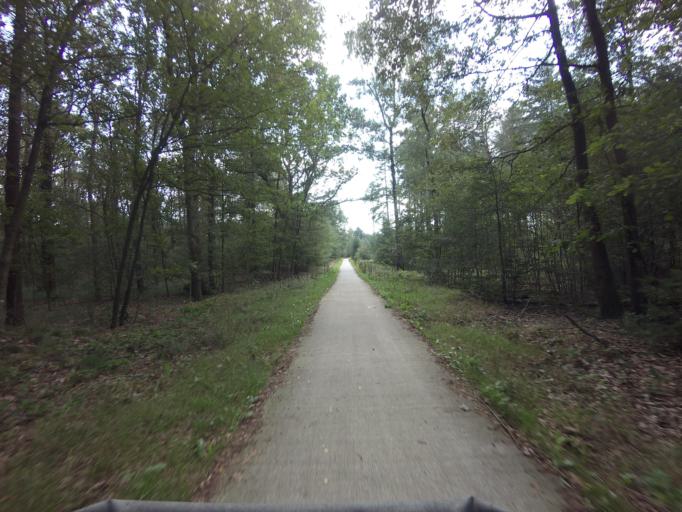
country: NL
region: Drenthe
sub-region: Gemeente Westerveld
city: Dwingeloo
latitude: 52.8379
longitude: 6.4758
